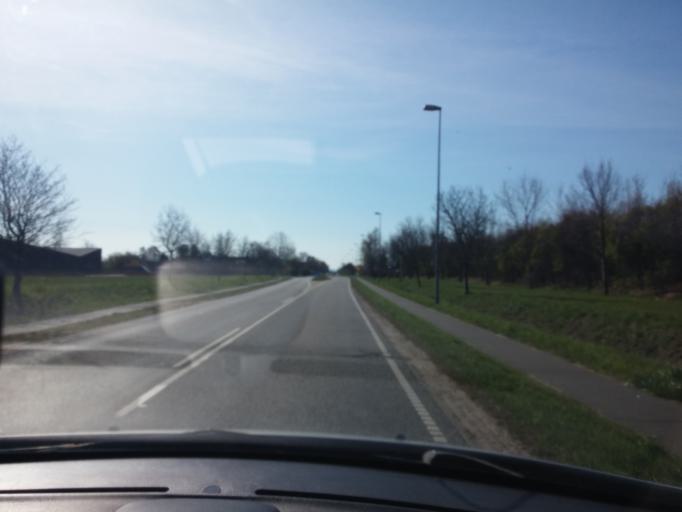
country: DK
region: Central Jutland
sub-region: Odder Kommune
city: Odder
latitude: 55.9212
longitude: 10.2474
